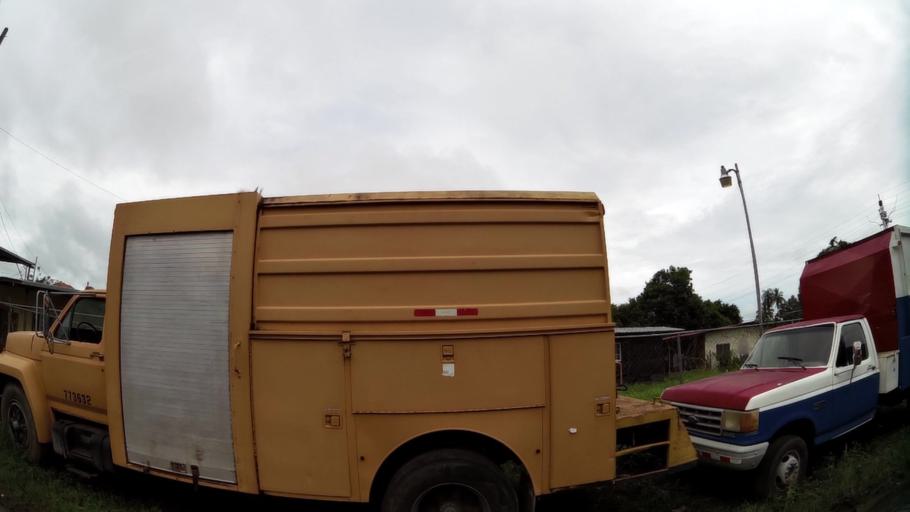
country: PA
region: Chiriqui
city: David
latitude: 8.4256
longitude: -82.4468
